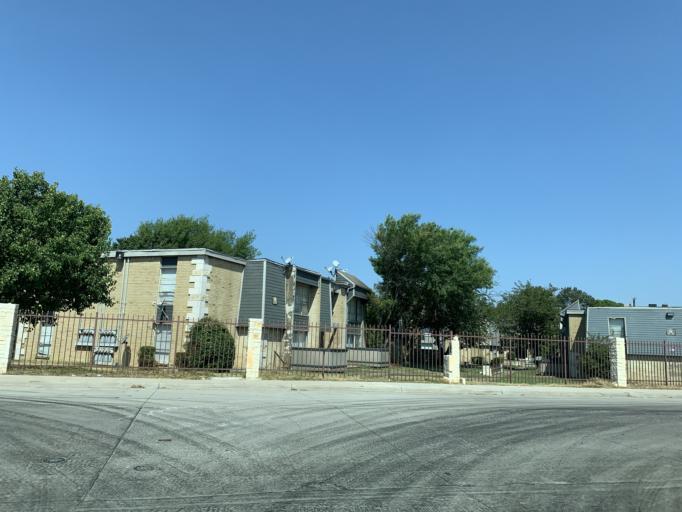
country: US
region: Texas
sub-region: Dallas County
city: Hutchins
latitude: 32.6717
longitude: -96.7599
